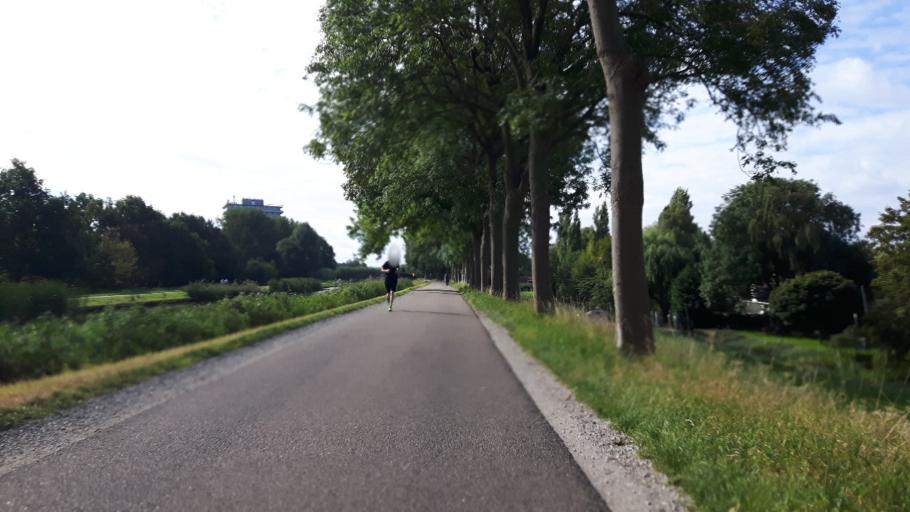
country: NL
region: North Holland
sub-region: Gemeente Purmerend
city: Purmerend
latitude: 52.5201
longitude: 4.9549
